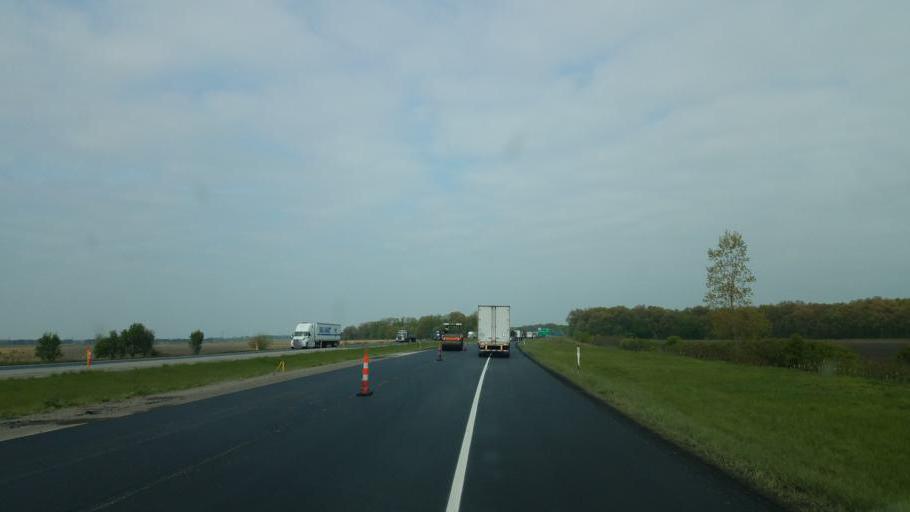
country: US
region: Indiana
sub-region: Saint Joseph County
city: Granger
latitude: 41.7316
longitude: -86.0911
